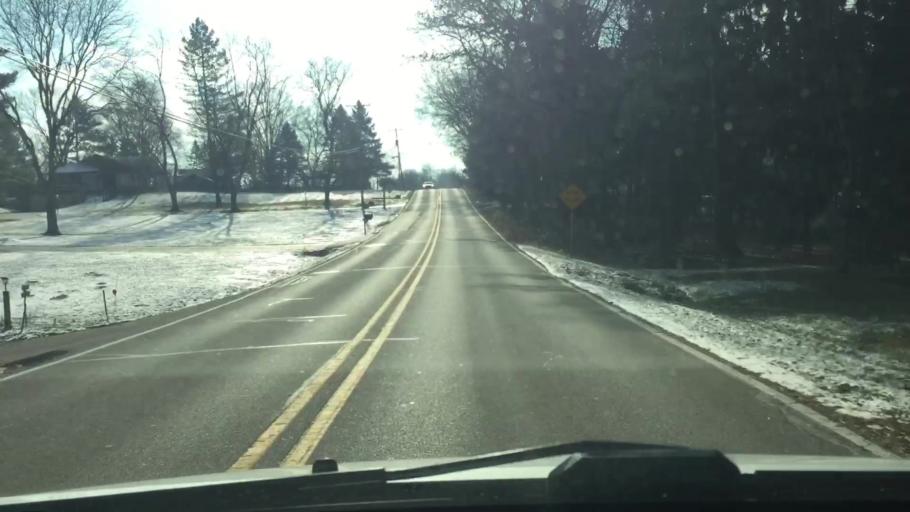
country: US
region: Wisconsin
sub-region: Waukesha County
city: Waukesha
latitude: 42.9792
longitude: -88.2873
